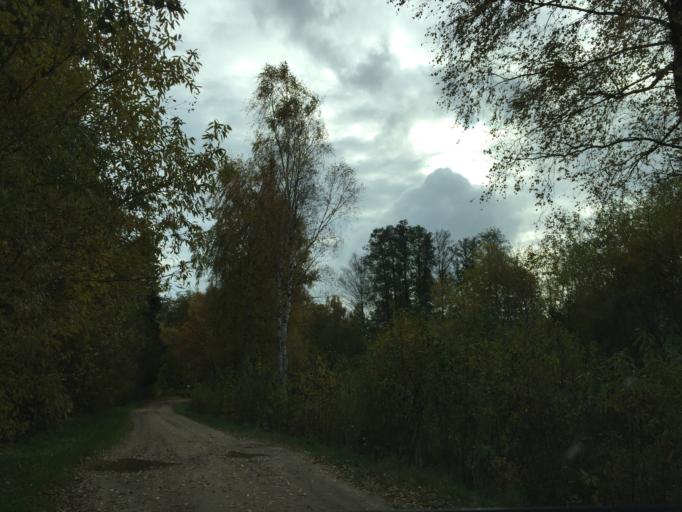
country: LV
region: Lielvarde
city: Lielvarde
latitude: 56.7322
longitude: 24.7861
